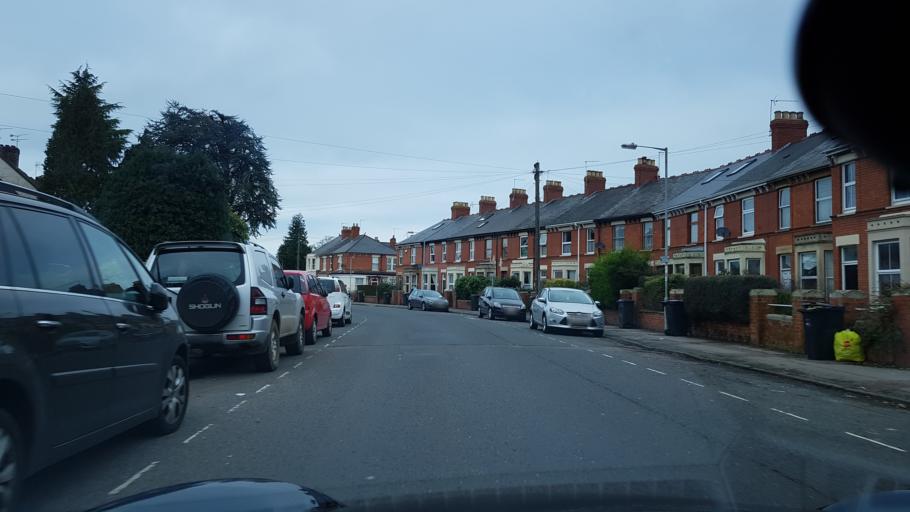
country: GB
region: England
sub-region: Somerset
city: Taunton
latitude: 51.0113
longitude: -3.0877
